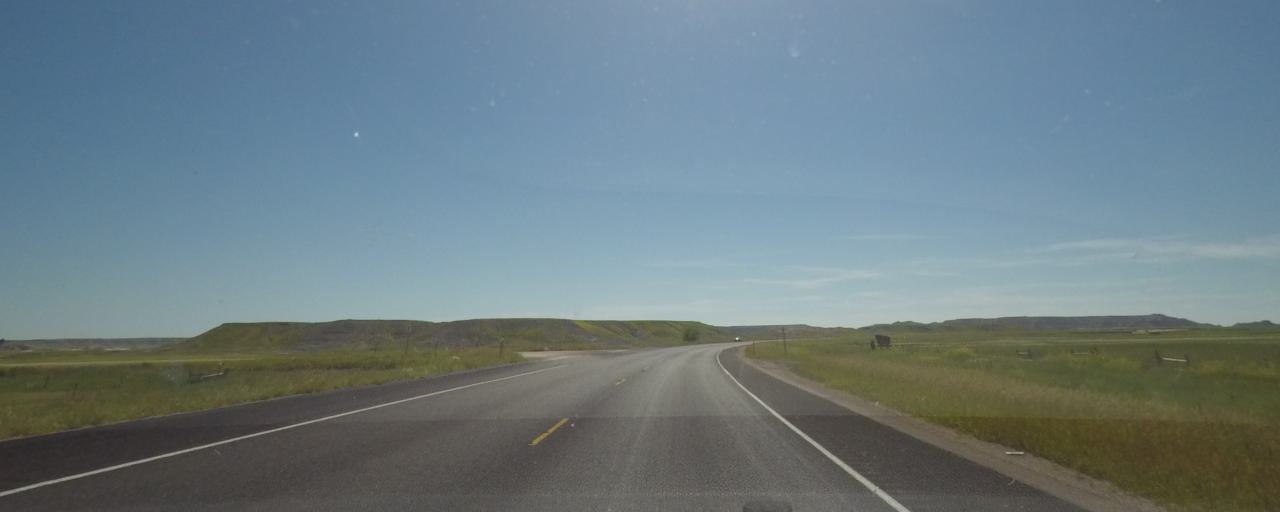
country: US
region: South Dakota
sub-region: Shannon County
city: Porcupine
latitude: 43.7782
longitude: -102.5382
